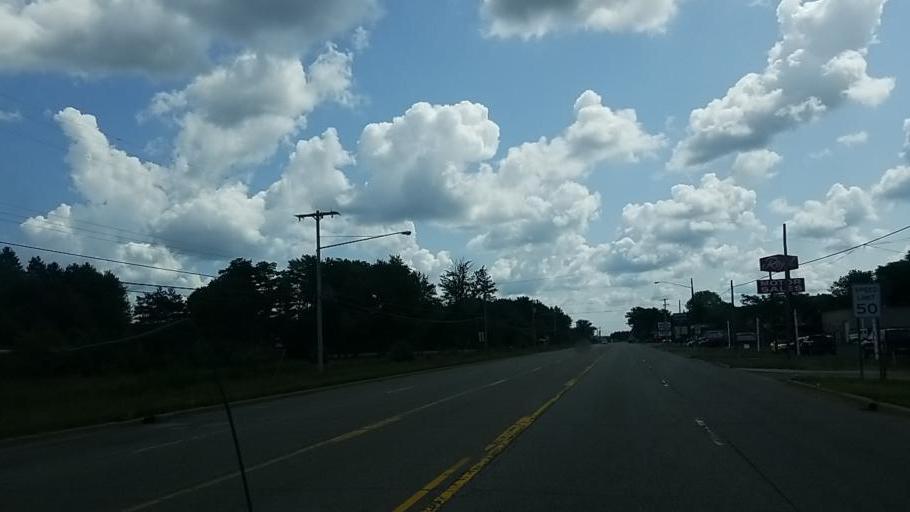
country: US
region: Michigan
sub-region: Muskegon County
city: Wolf Lake
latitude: 43.2342
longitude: -86.1533
